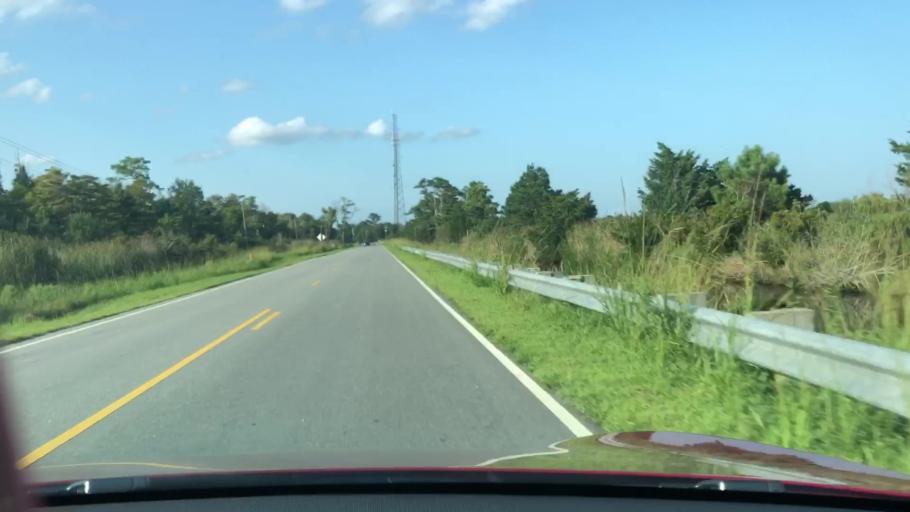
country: US
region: North Carolina
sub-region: Dare County
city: Wanchese
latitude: 35.7025
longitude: -75.7705
